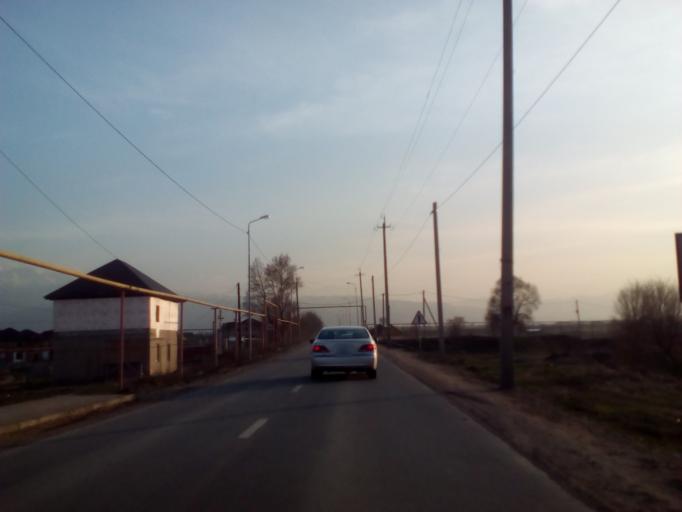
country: KZ
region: Almaty Oblysy
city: Burunday
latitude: 43.2394
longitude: 76.7449
